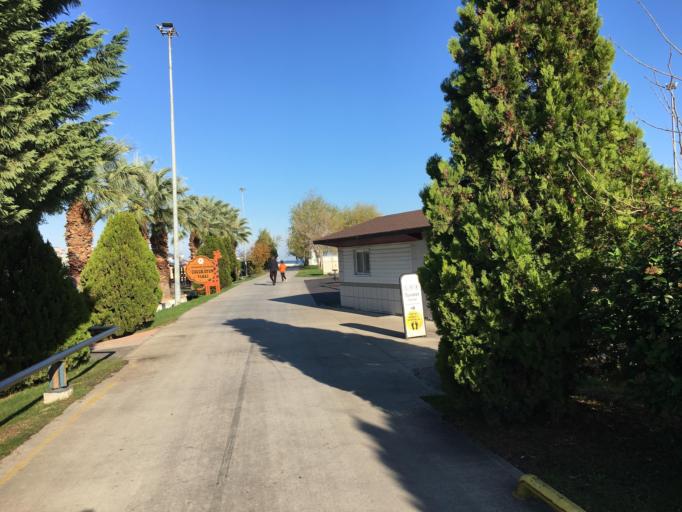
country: TR
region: Samsun
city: Samsun
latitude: 41.2857
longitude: 36.3455
